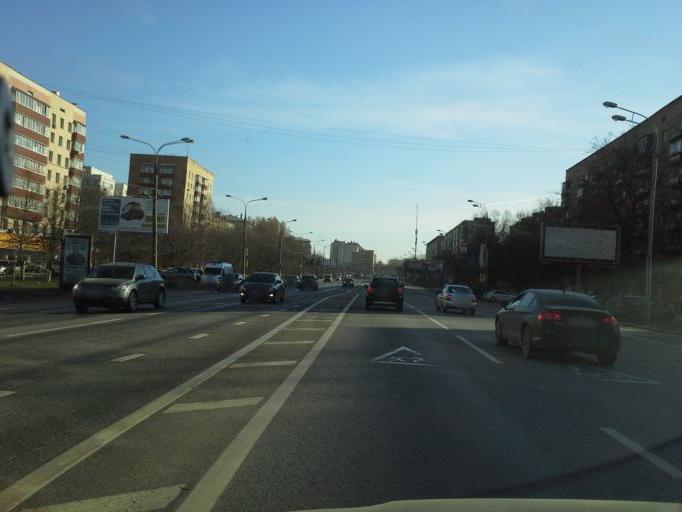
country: RU
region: Moscow
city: Taganskiy
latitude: 55.7225
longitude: 37.6636
